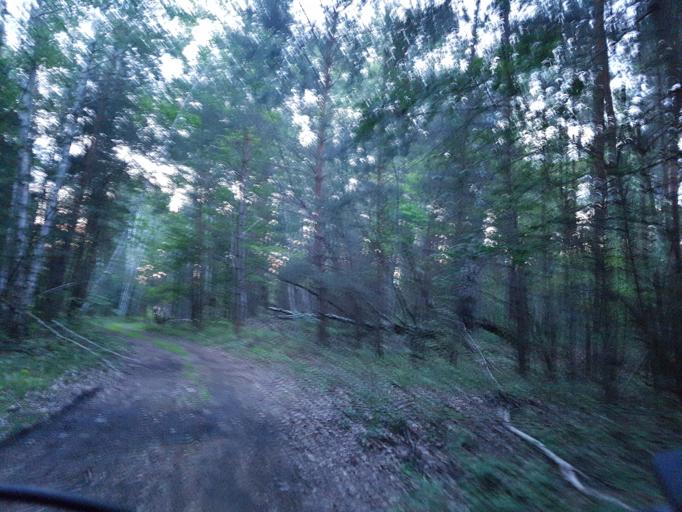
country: DE
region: Brandenburg
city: Trobitz
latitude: 51.5824
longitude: 13.4203
